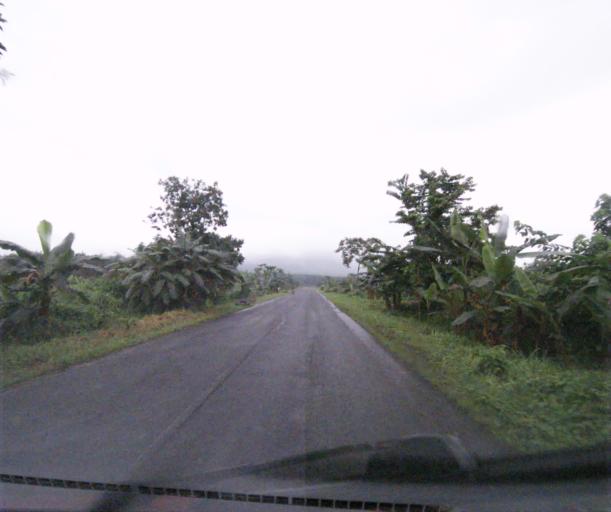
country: CM
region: South-West Province
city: Idenao
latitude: 4.2041
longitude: 8.9975
